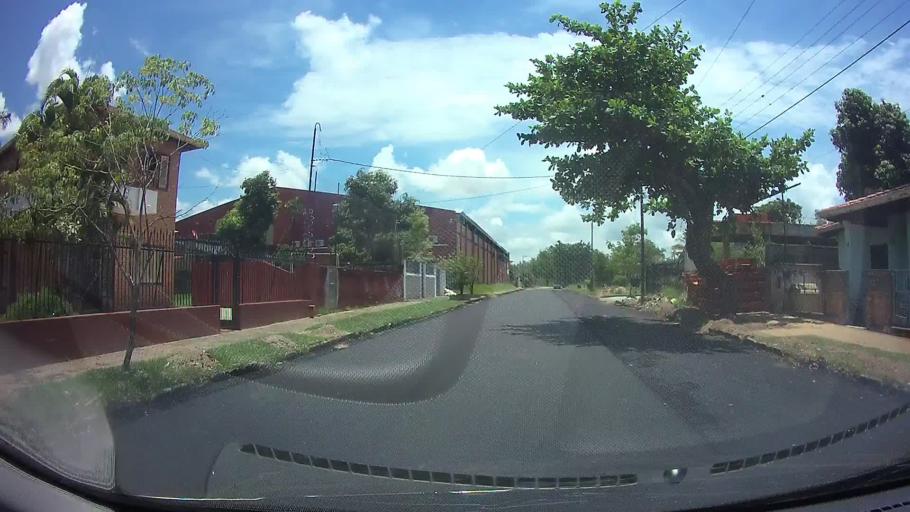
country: PY
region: Central
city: San Lorenzo
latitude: -25.2638
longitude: -57.5015
